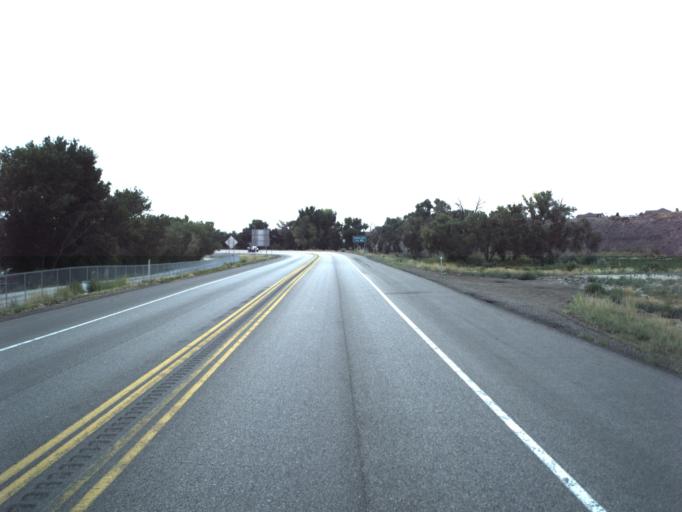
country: US
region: Utah
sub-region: Carbon County
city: Price
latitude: 39.5937
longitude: -110.8216
